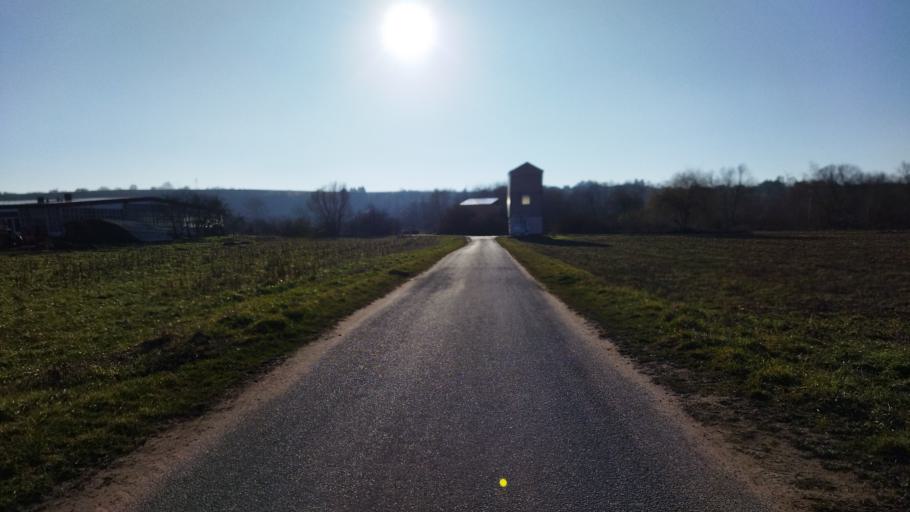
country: DE
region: Bavaria
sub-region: Regierungsbezirk Unterfranken
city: Albertshofen
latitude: 49.7635
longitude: 10.1596
